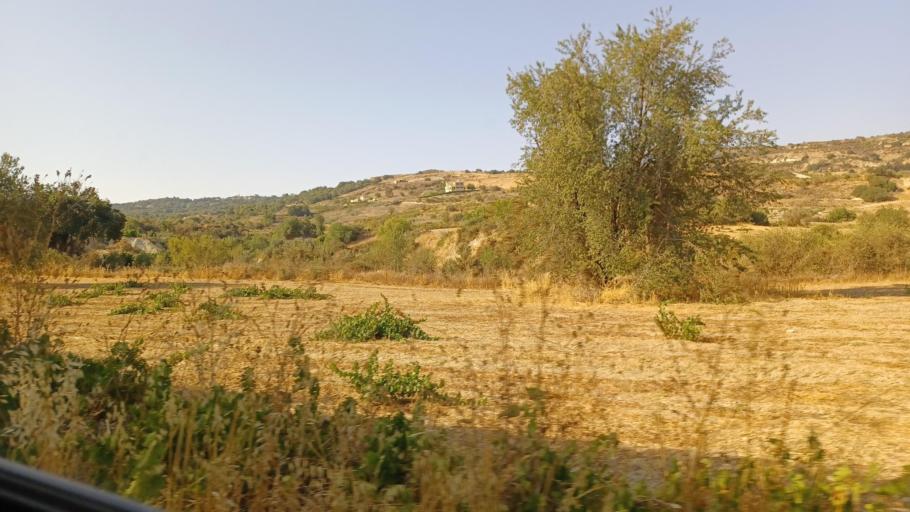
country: CY
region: Pafos
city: Tala
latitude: 34.9113
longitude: 32.4824
